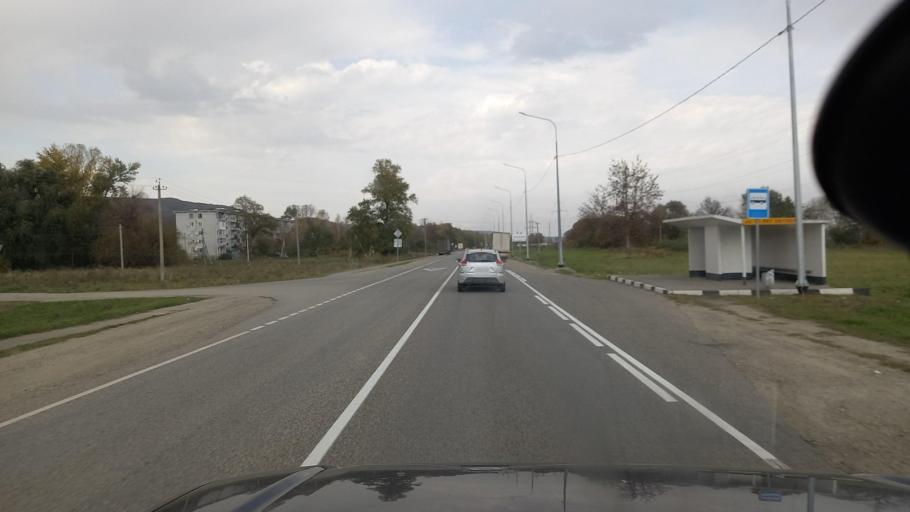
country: RU
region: Krasnodarskiy
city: Shedok
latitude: 44.1765
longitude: 40.8411
